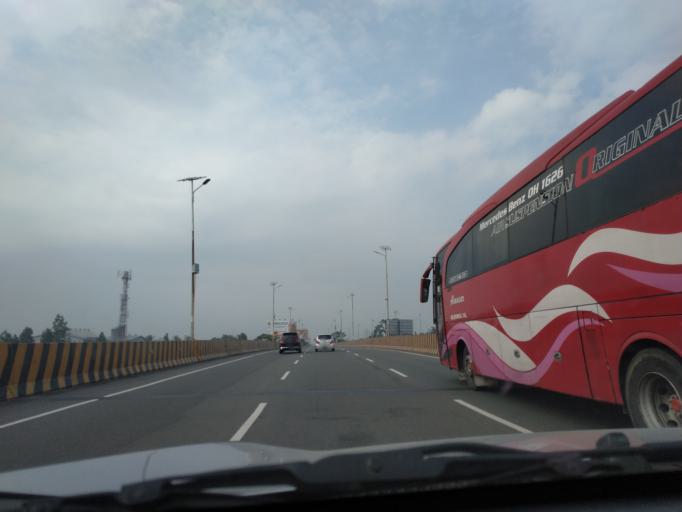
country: ID
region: North Sumatra
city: Percut
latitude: 3.6099
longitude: 98.8539
